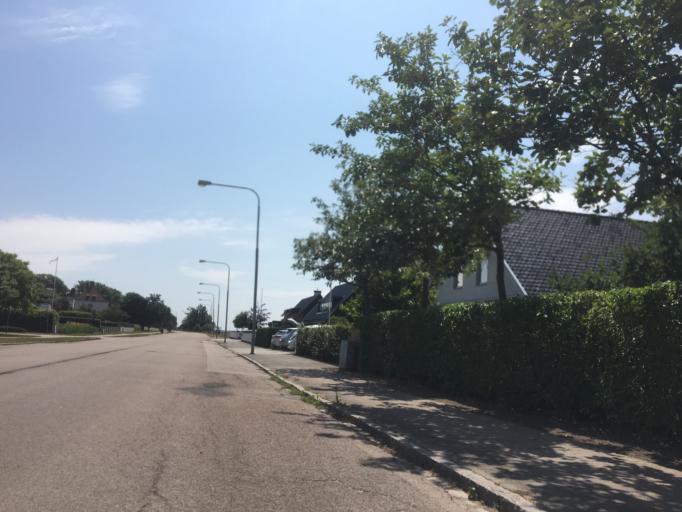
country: SE
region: Skane
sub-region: Landskrona
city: Landskrona
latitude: 55.8875
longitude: 12.8108
